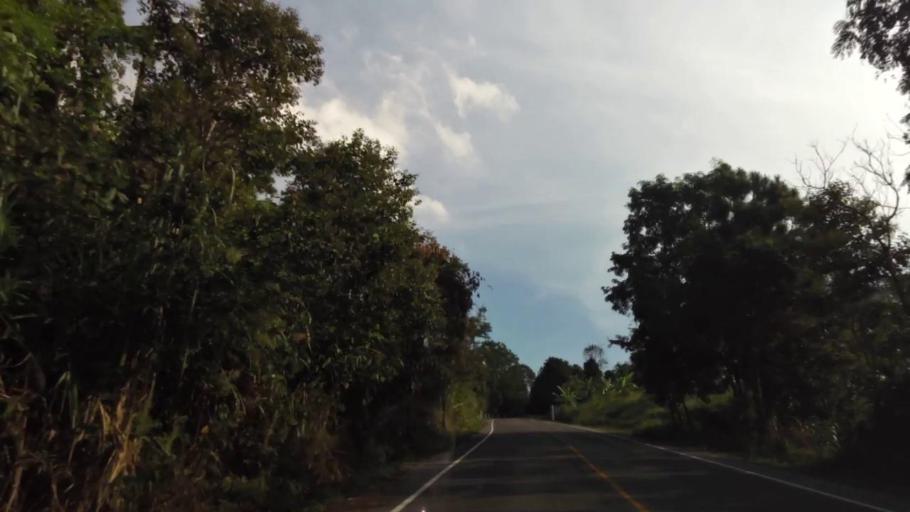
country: TH
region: Chiang Rai
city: Khun Tan
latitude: 19.8729
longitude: 100.3212
